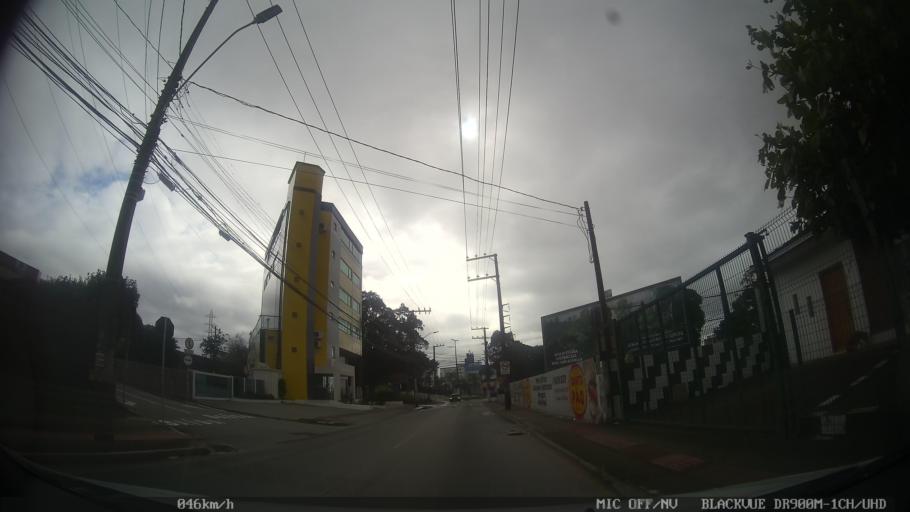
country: BR
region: Santa Catarina
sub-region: Sao Jose
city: Campinas
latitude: -27.5858
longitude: -48.6194
